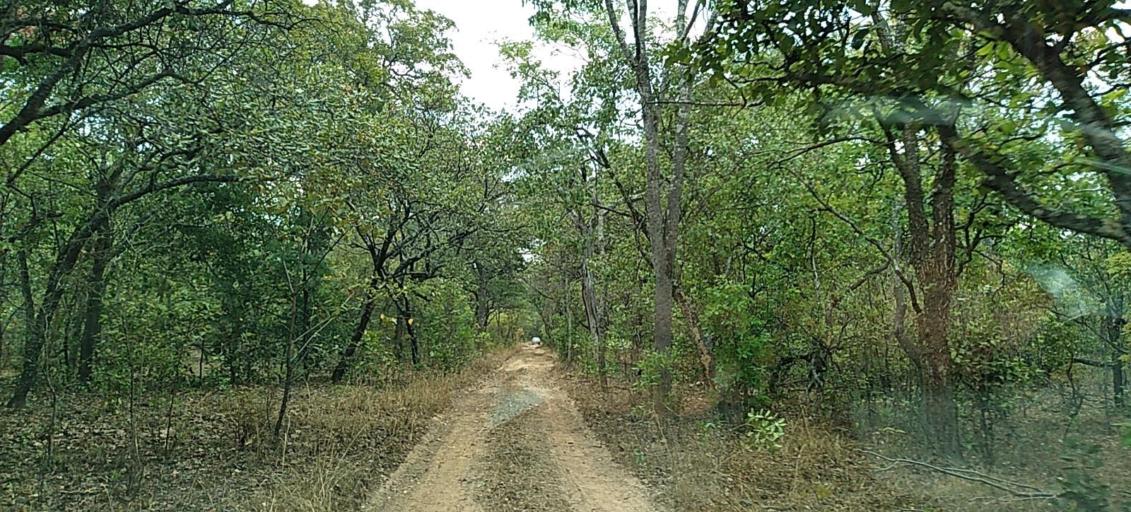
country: ZM
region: Copperbelt
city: Chililabombwe
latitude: -12.4735
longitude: 27.7004
